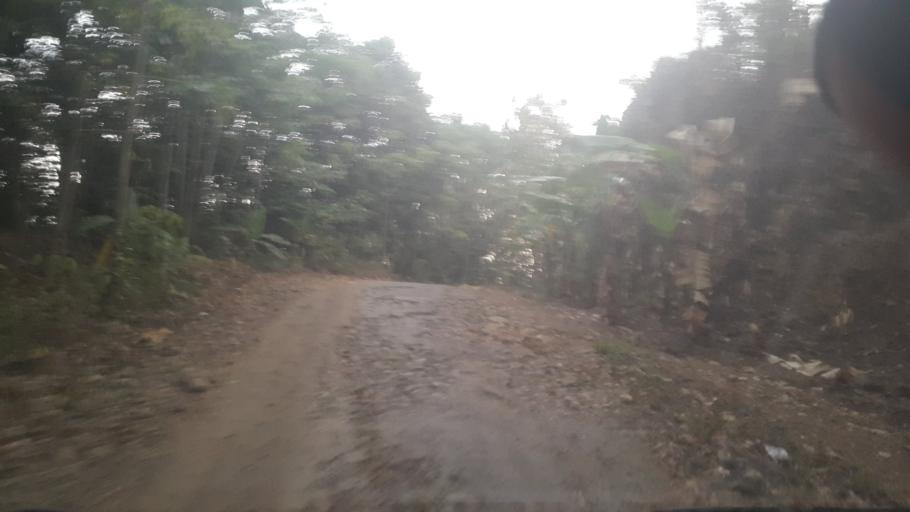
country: ID
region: West Java
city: Bojonggaling
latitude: -6.9582
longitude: 106.6041
